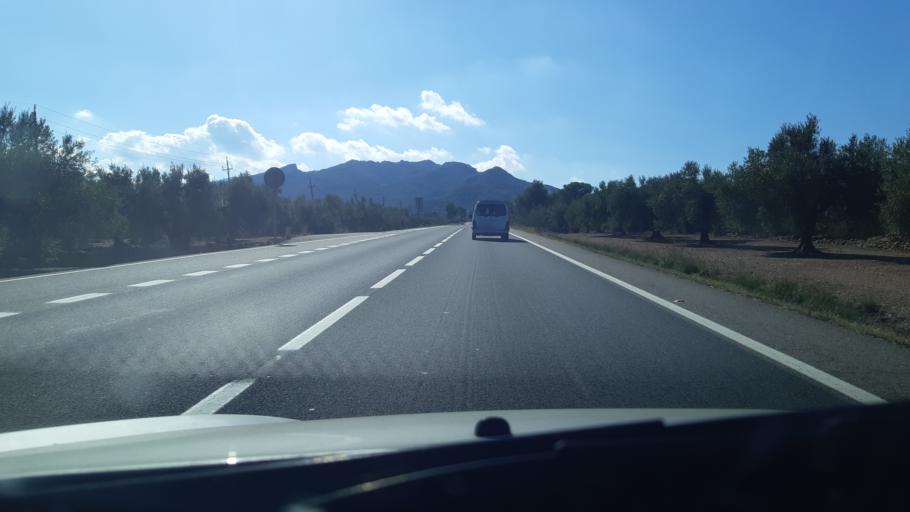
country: ES
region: Catalonia
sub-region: Provincia de Tarragona
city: Rasquera
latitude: 41.0122
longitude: 0.6097
